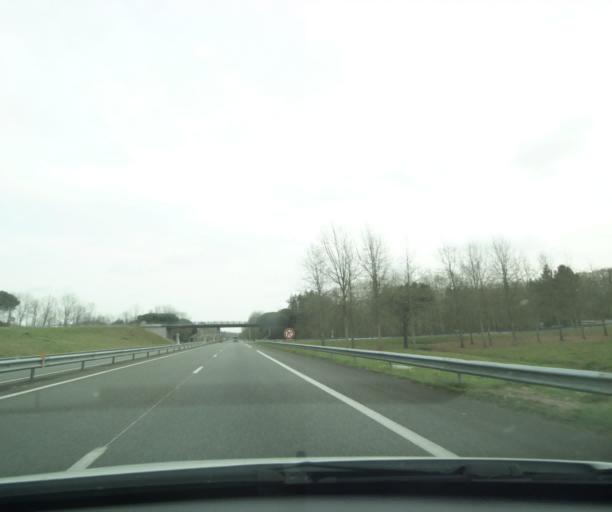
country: FR
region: Aquitaine
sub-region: Departement des Landes
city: Peyrehorade
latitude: 43.5283
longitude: -1.1512
